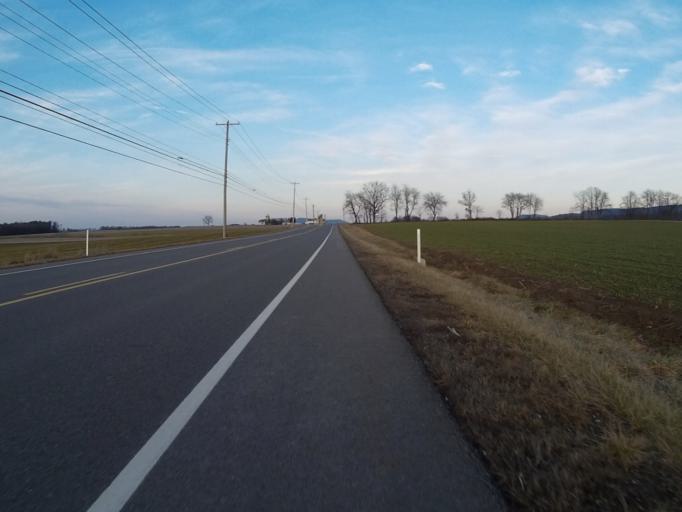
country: US
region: Pennsylvania
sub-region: Centre County
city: Pine Grove Mills
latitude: 40.7394
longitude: -77.9146
